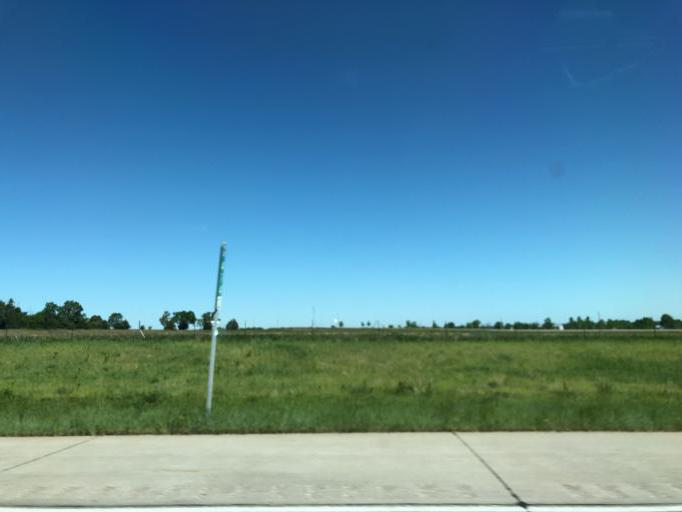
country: US
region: Nebraska
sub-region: Lancaster County
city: Waverly
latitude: 40.9115
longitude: -96.4860
